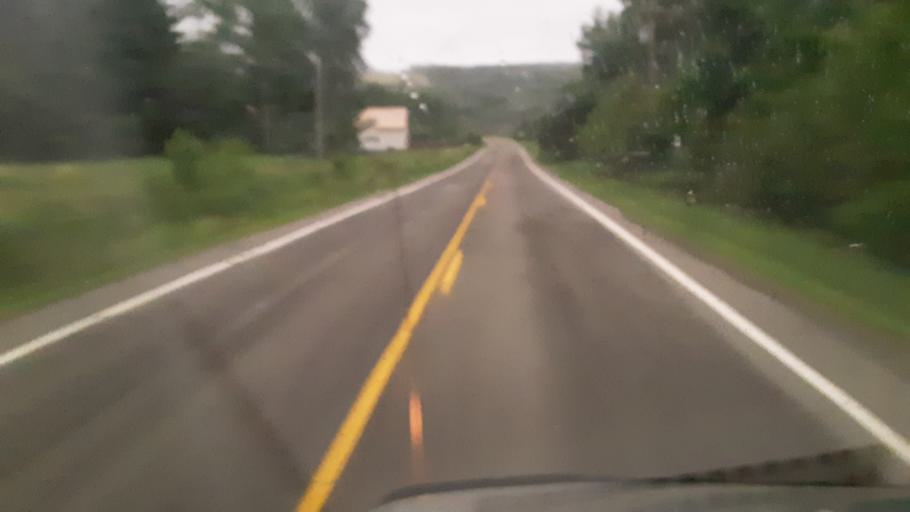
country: US
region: Maine
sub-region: Penobscot County
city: Patten
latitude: 46.0580
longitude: -68.4404
